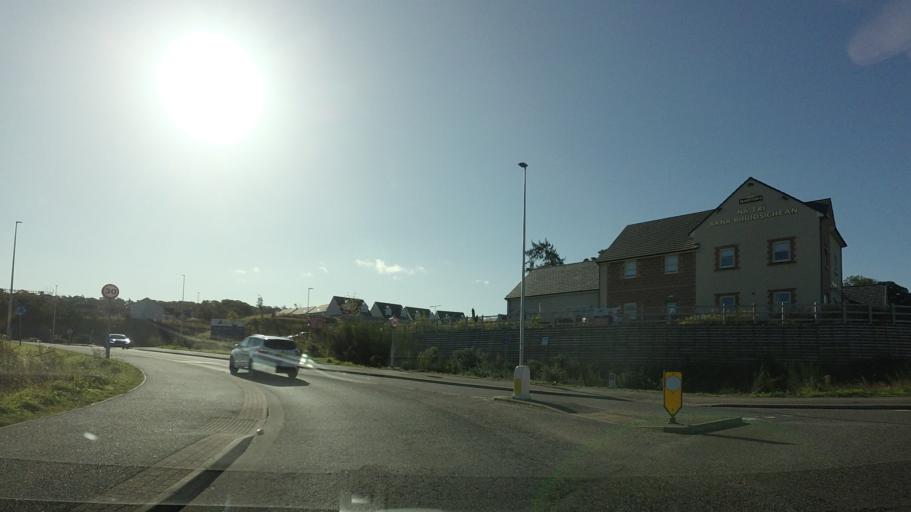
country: GB
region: Scotland
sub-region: Highland
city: Inverness
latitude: 57.4502
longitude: -4.2182
